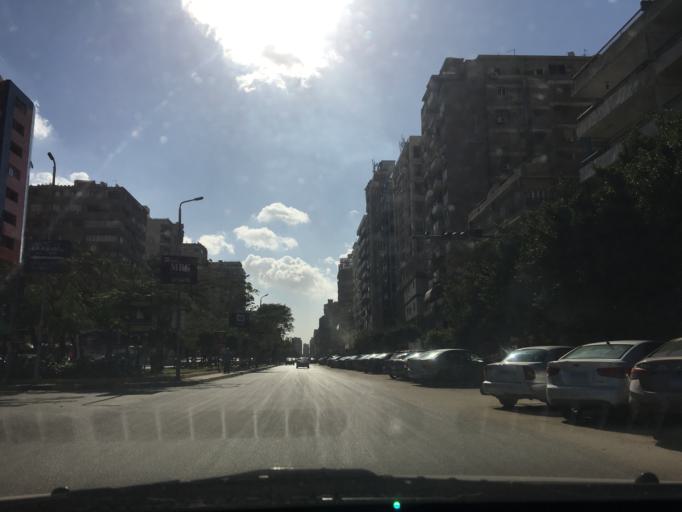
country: EG
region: Muhafazat al Qahirah
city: Cairo
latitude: 30.0604
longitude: 31.3452
